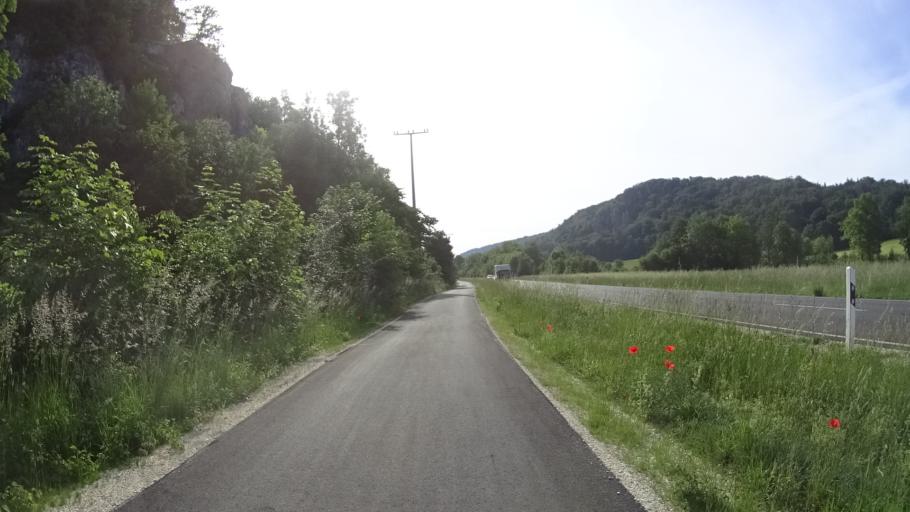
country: DE
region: Bavaria
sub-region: Lower Bavaria
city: Essing
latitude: 48.9274
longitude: 11.8203
